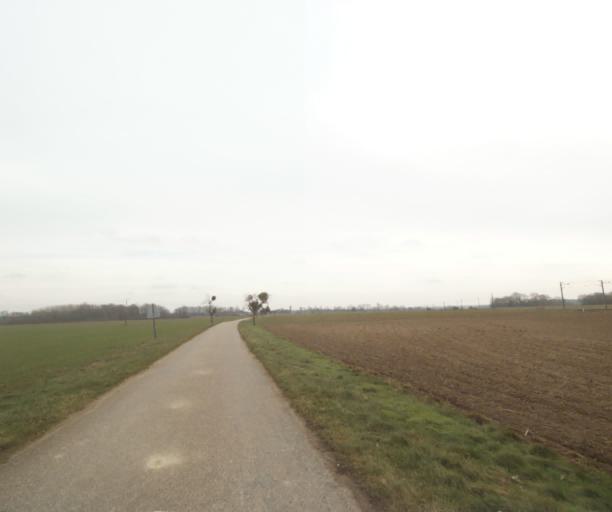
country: FR
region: Champagne-Ardenne
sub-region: Departement de la Haute-Marne
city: Villiers-en-Lieu
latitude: 48.6730
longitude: 4.8796
